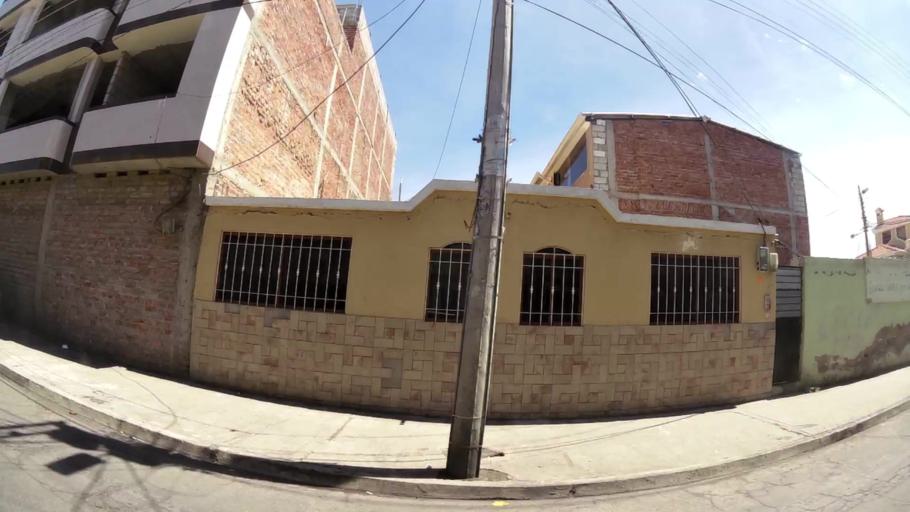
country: EC
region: Chimborazo
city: Riobamba
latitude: -1.6759
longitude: -78.6554
